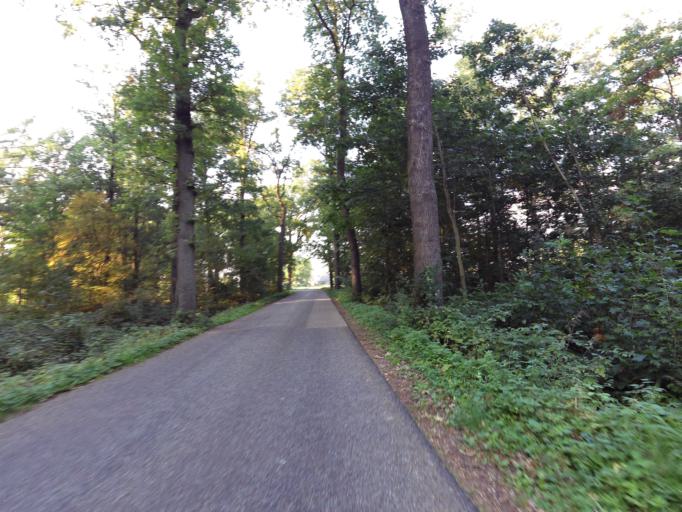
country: NL
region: Gelderland
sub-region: Oude IJsselstreek
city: Wisch
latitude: 51.9372
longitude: 6.3888
